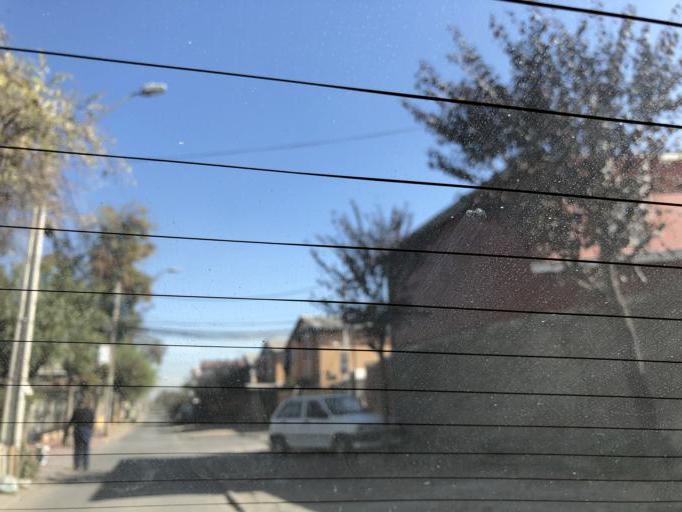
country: CL
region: Santiago Metropolitan
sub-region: Provincia de Cordillera
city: Puente Alto
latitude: -33.6119
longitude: -70.5891
